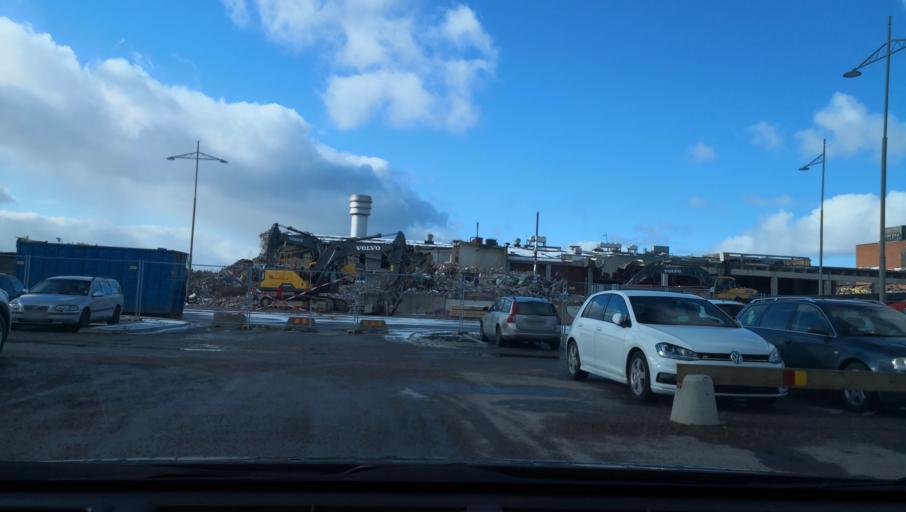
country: SE
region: Vaestmanland
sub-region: Vasteras
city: Vasteras
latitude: 59.6361
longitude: 16.5681
